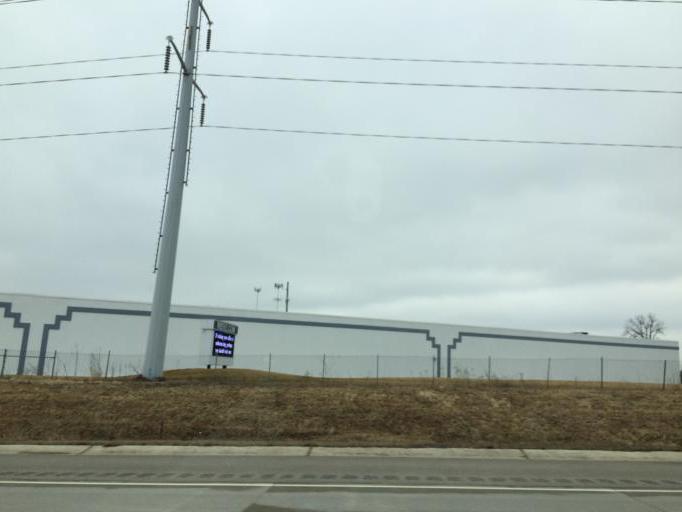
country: US
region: Illinois
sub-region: Kane County
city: Sleepy Hollow
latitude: 42.0757
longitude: -88.3244
